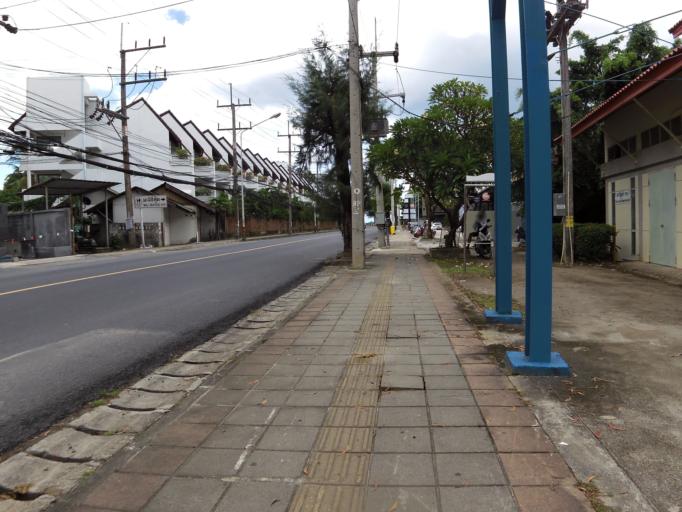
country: TH
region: Phuket
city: Ban Karon
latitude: 7.8510
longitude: 98.2943
